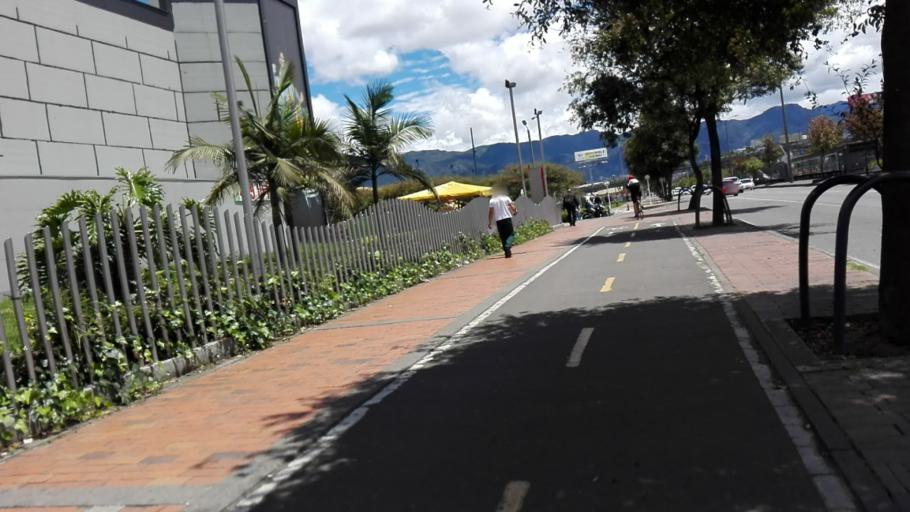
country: CO
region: Bogota D.C.
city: Barrio San Luis
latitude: 4.6920
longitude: -74.0852
